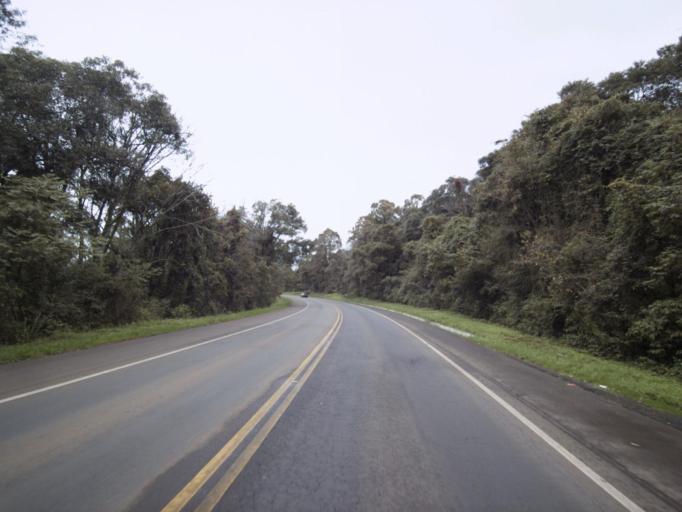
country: BR
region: Santa Catarina
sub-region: Concordia
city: Concordia
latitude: -27.2634
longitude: -51.9580
